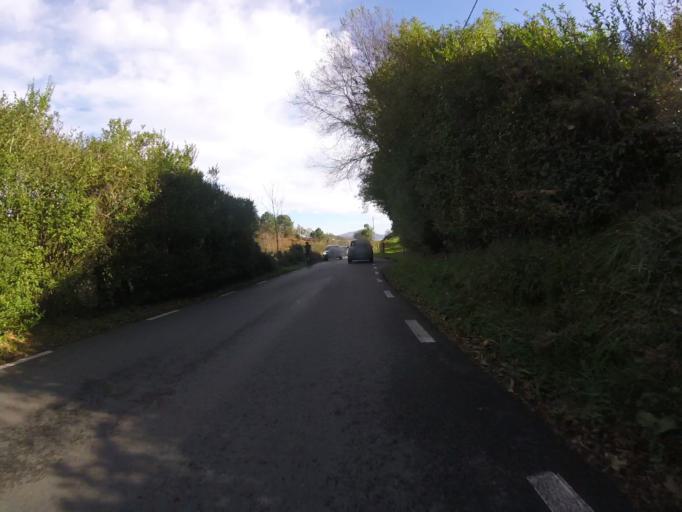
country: ES
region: Basque Country
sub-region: Provincia de Guipuzcoa
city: Usurbil
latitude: 43.3015
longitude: -2.0546
